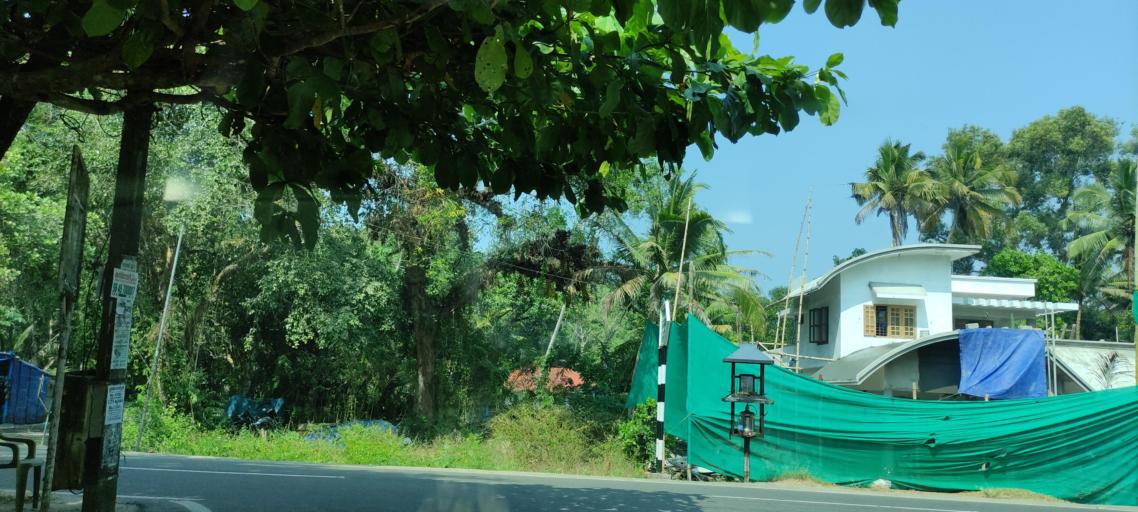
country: IN
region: Kerala
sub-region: Alappuzha
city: Shertallai
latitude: 9.6017
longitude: 76.3115
